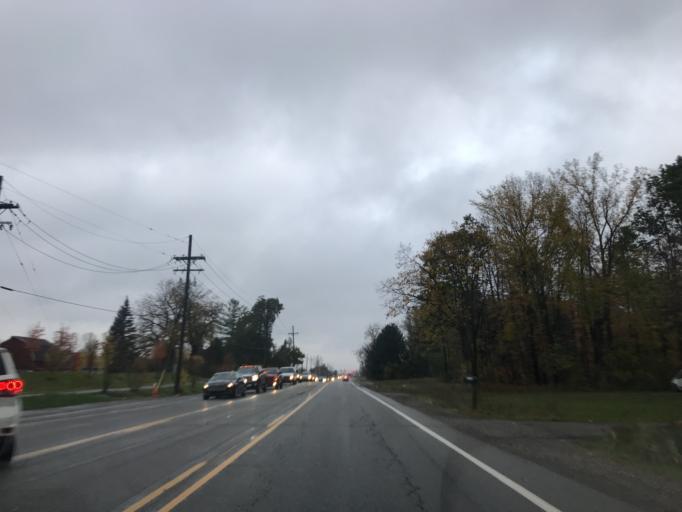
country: US
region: Michigan
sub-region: Oakland County
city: Novi
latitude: 42.4806
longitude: -83.5152
